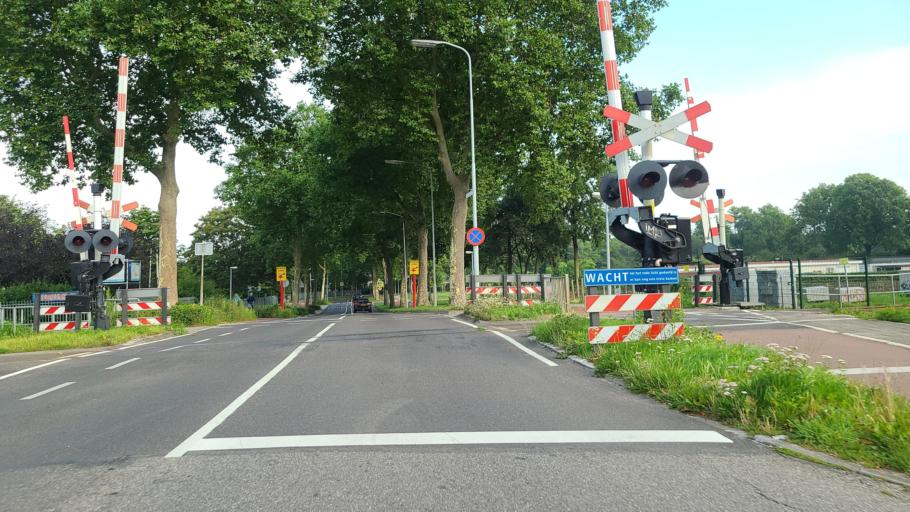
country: NL
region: Gelderland
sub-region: Gemeente Tiel
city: Tiel
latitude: 51.8935
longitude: 5.4306
